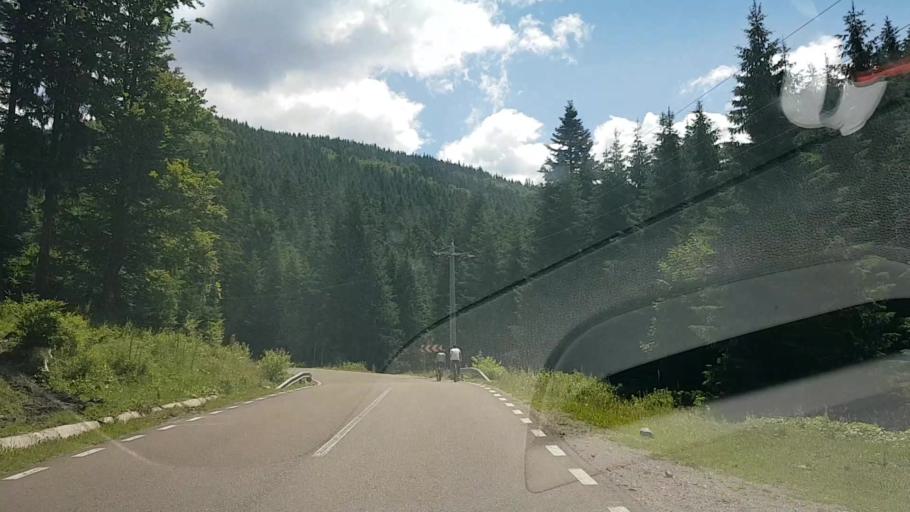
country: RO
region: Suceava
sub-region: Comuna Sadova
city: Sadova
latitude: 47.4719
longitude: 25.5093
